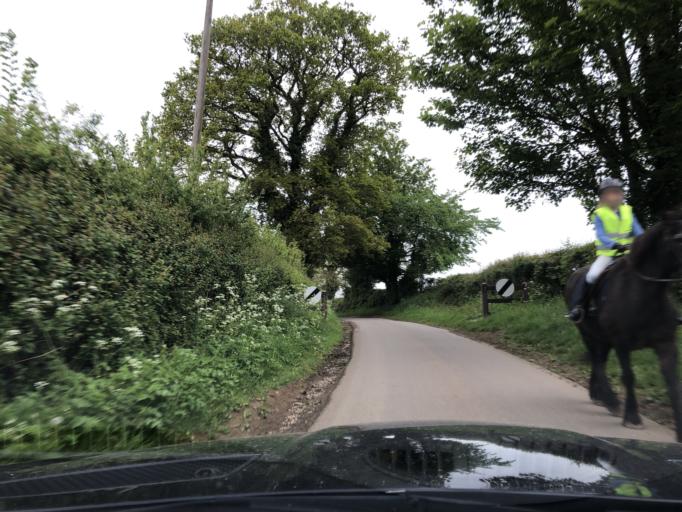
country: GB
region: England
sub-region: Oxfordshire
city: Claydon
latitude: 52.1440
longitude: -1.3723
